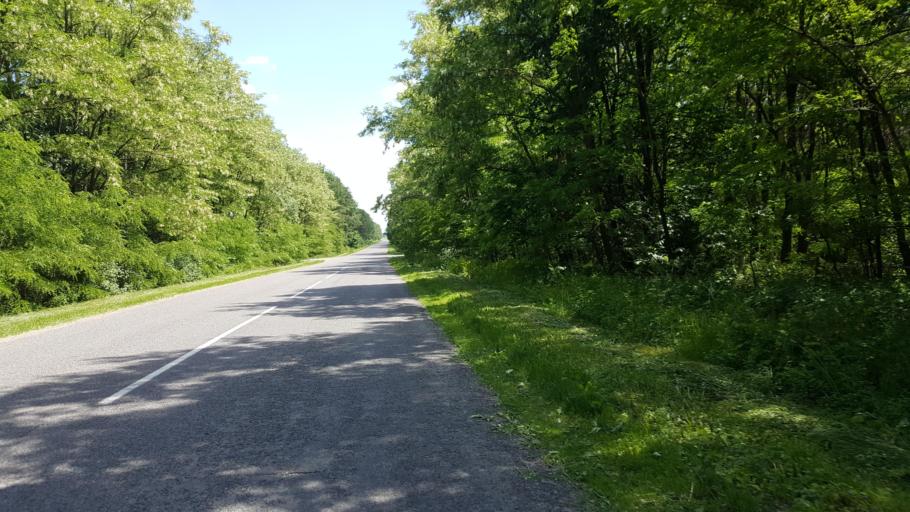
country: BY
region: Brest
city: Kobryn
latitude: 52.2277
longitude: 24.2375
